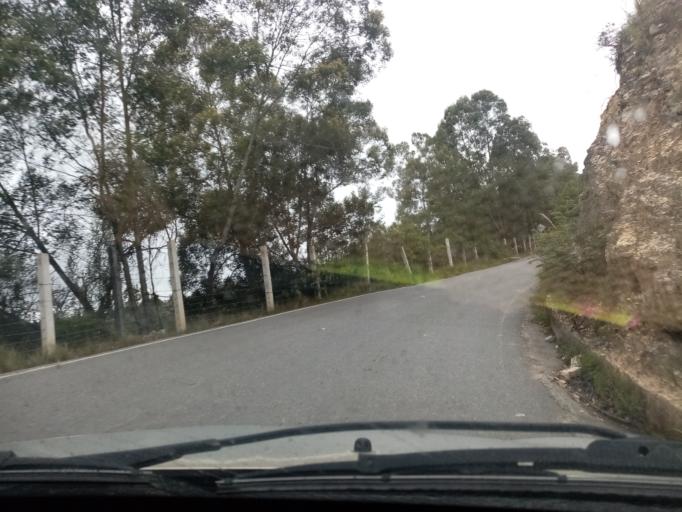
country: CO
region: Boyaca
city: Siachoque
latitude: 5.5695
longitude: -73.2534
